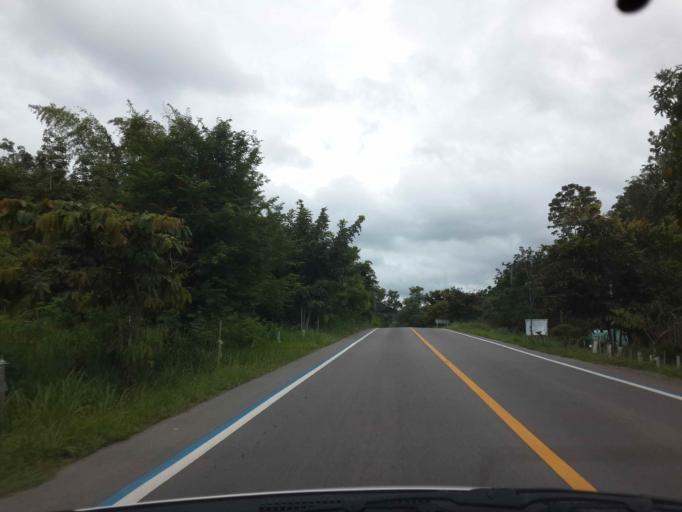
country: TH
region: Ratchaburi
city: Suan Phueng
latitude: 13.5969
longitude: 99.2336
